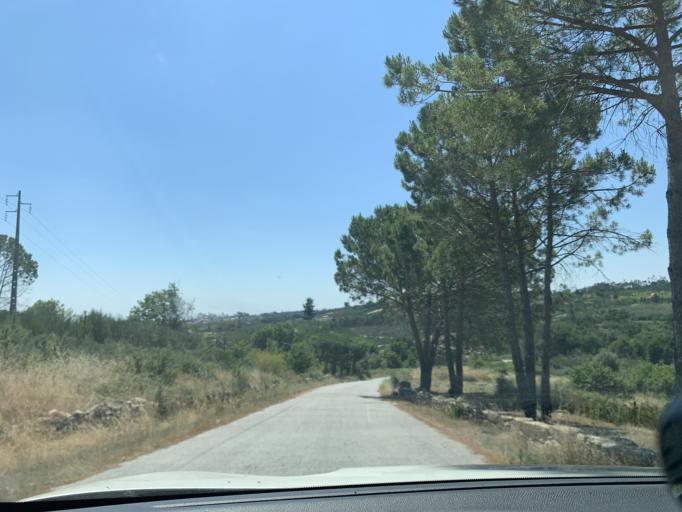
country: PT
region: Viseu
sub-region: Mangualde
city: Mangualde
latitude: 40.5555
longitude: -7.7305
